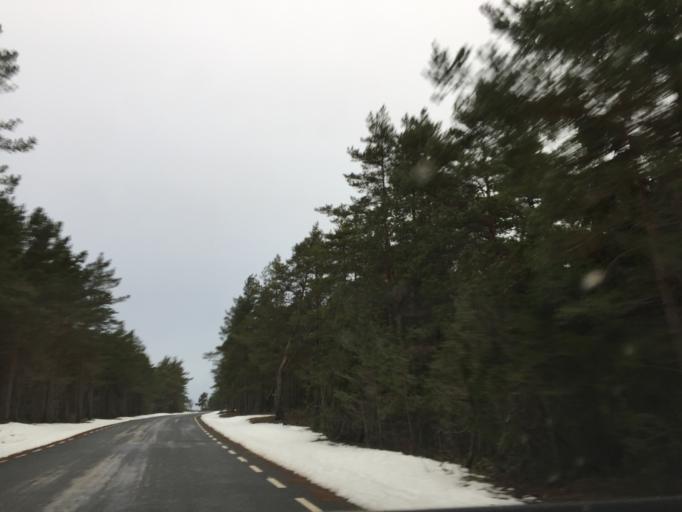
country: EE
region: Saare
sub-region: Kuressaare linn
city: Kuressaare
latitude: 58.5696
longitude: 22.2964
